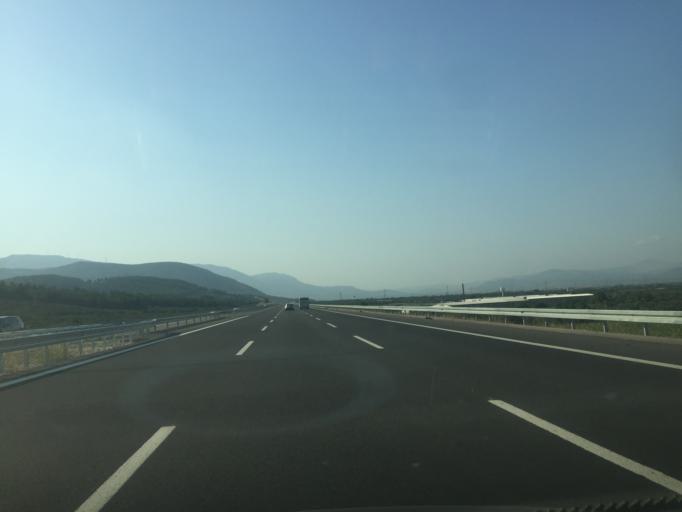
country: TR
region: Manisa
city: Zeytinliova
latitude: 39.0446
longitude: 27.7389
